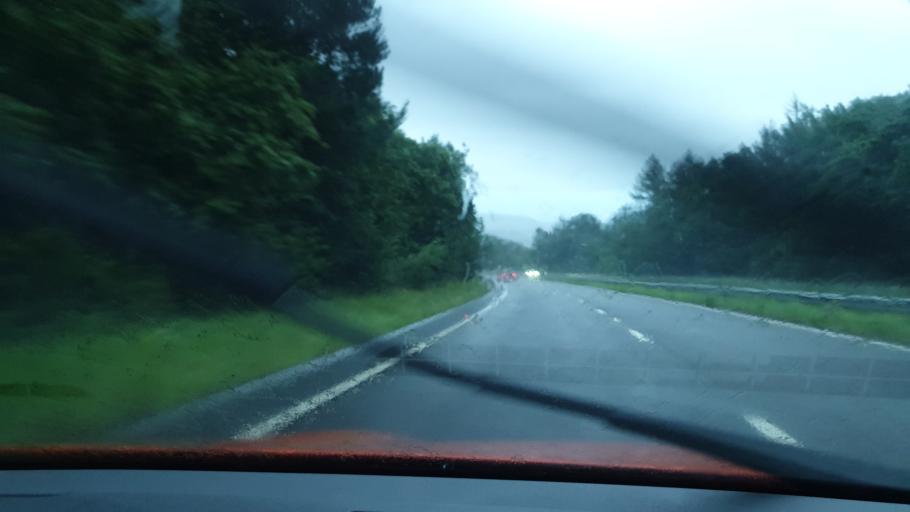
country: GB
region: England
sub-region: Cumbria
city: Grange-over-Sands
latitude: 54.2205
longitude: -2.9023
